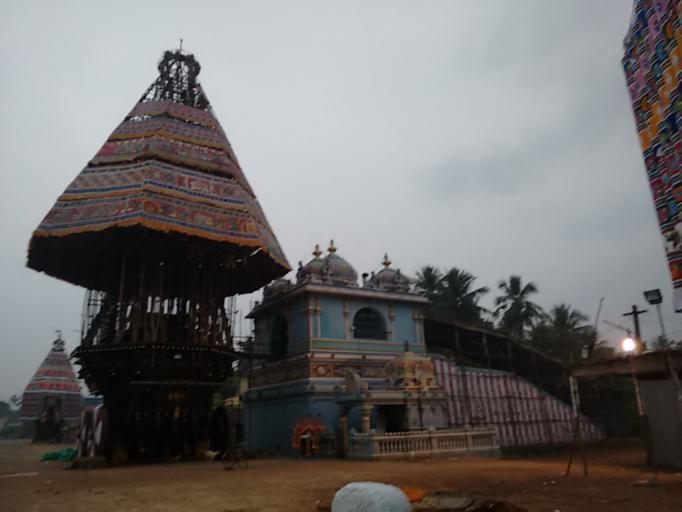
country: IN
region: Tamil Nadu
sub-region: Thanjavur
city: Thiruvidaimaruthur
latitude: 10.9962
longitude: 79.4558
